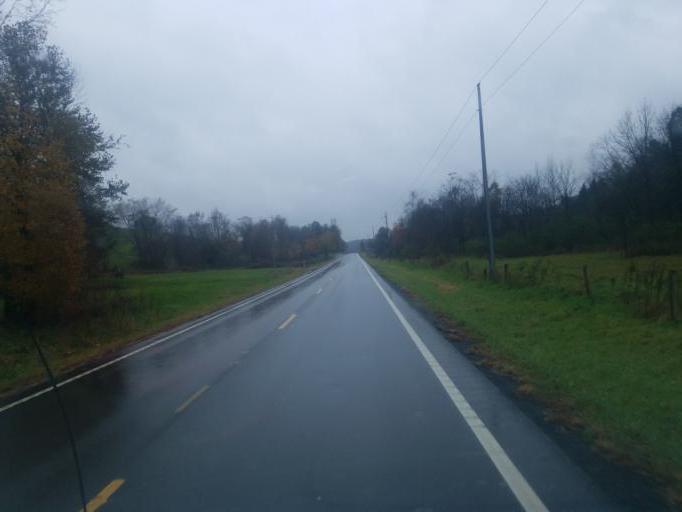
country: US
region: Ohio
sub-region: Muskingum County
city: Frazeysburg
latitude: 40.1873
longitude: -82.2303
